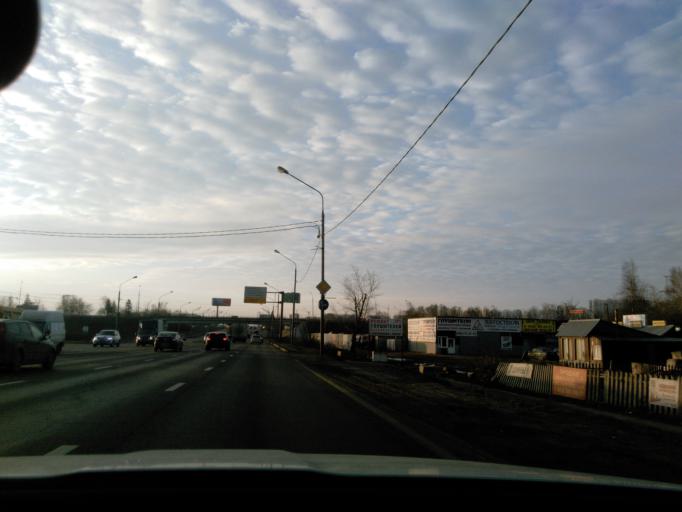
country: RU
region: Moscow
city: Khimki
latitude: 55.9225
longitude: 37.3899
